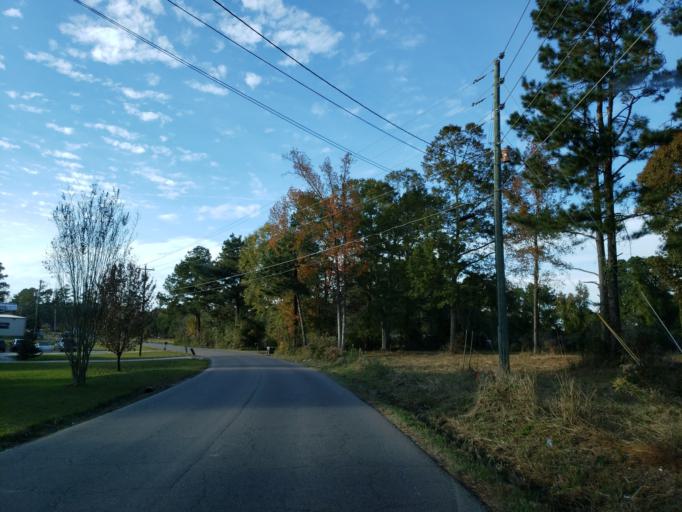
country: US
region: Mississippi
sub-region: Lamar County
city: West Hattiesburg
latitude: 31.3024
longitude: -89.3786
